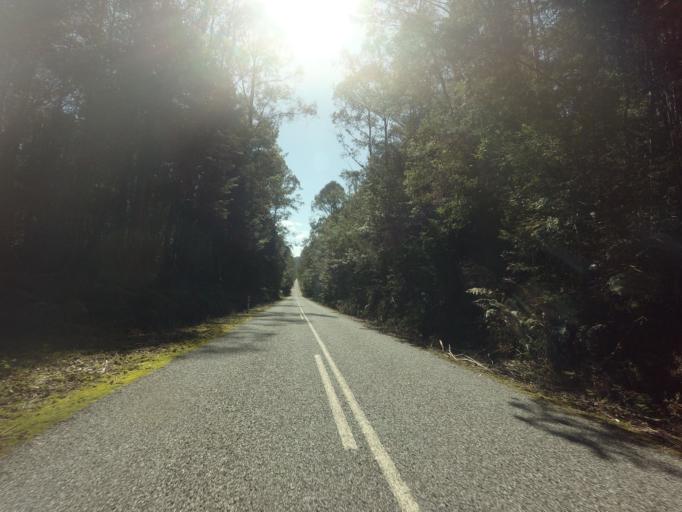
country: AU
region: Tasmania
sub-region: Derwent Valley
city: New Norfolk
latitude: -42.7444
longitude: 146.4156
